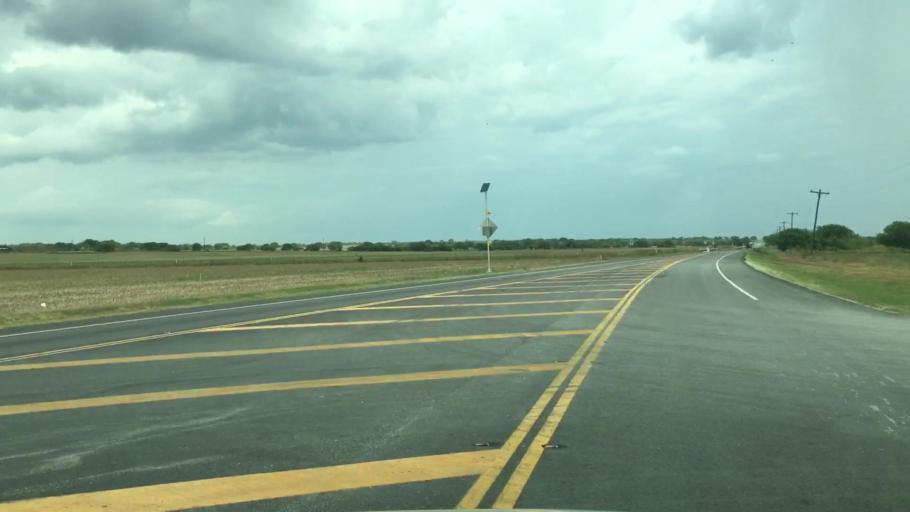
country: US
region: Texas
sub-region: Live Oak County
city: George West
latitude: 28.3381
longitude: -98.0221
